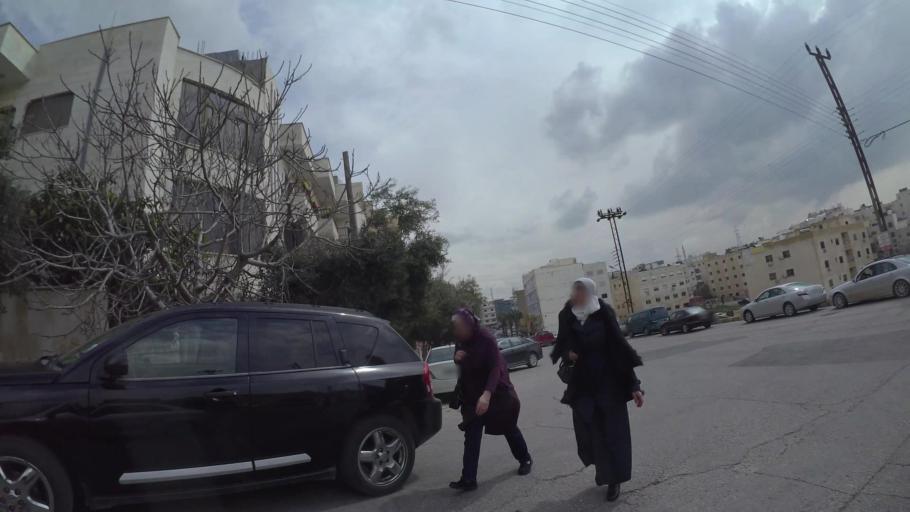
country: JO
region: Amman
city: Umm as Summaq
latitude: 31.8962
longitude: 35.8375
